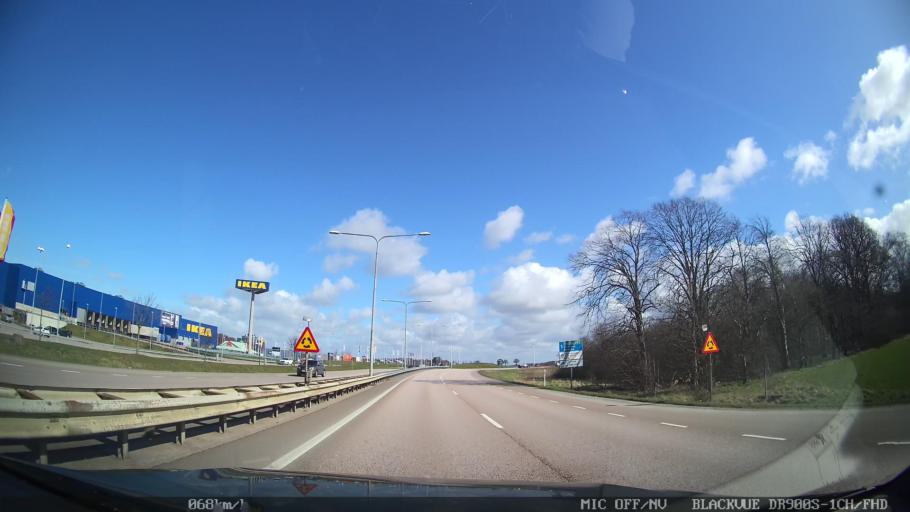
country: SE
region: Skane
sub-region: Helsingborg
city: Odakra
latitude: 56.0916
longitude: 12.7602
